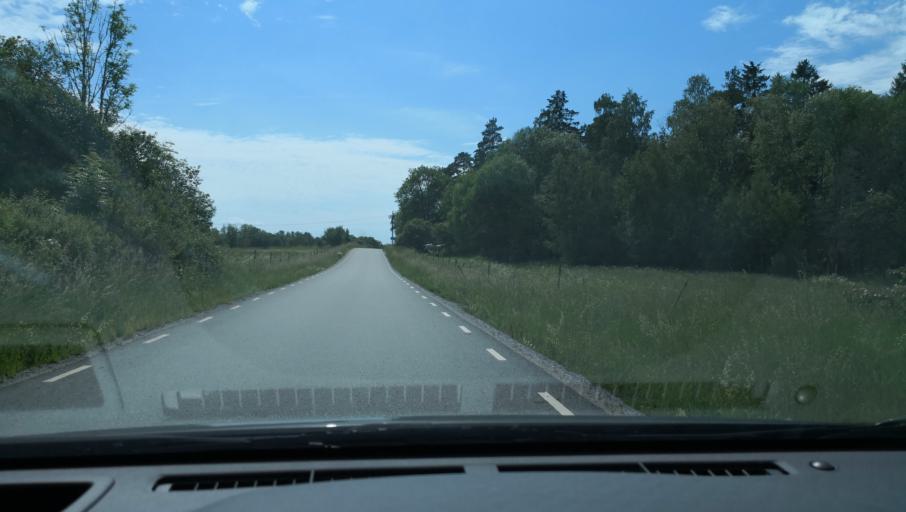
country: SE
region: Uppsala
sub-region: Habo Kommun
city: Balsta
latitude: 59.6890
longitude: 17.4653
